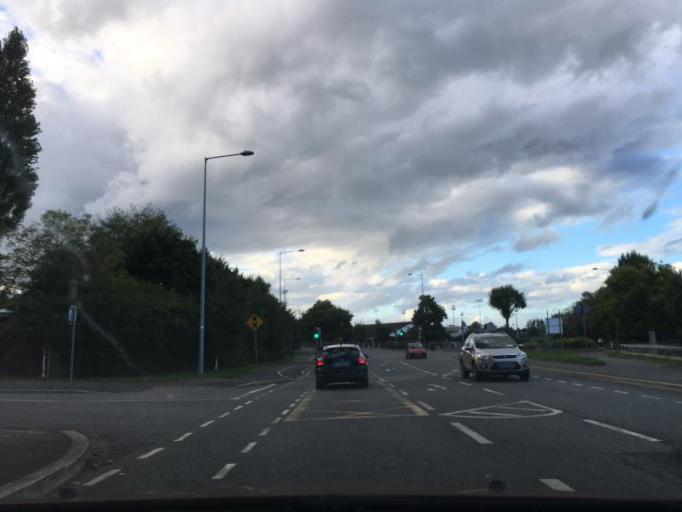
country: IE
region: Leinster
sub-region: Wicklow
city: Wicklow
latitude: 52.9837
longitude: -6.0518
